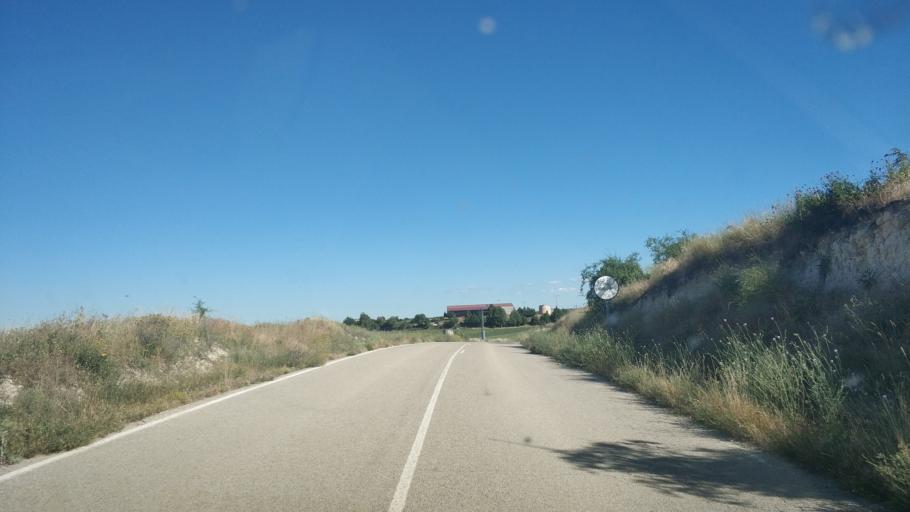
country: ES
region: Castille and Leon
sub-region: Provincia de Soria
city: Liceras
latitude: 41.4657
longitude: -3.2157
